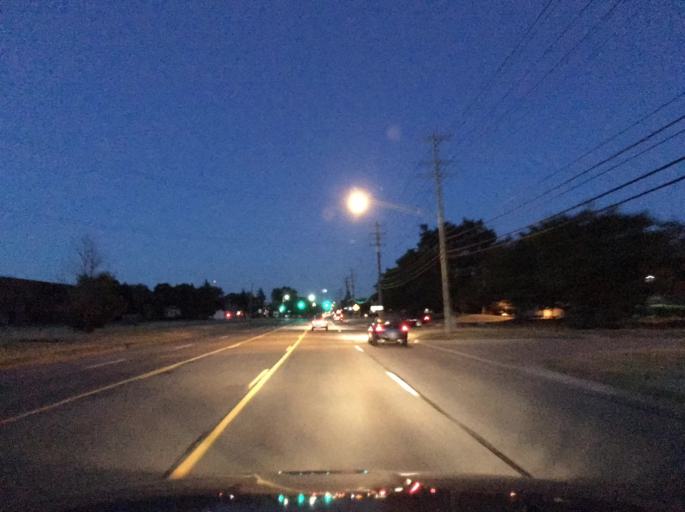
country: US
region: Michigan
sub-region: Macomb County
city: Fraser
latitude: 42.5392
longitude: -82.9323
